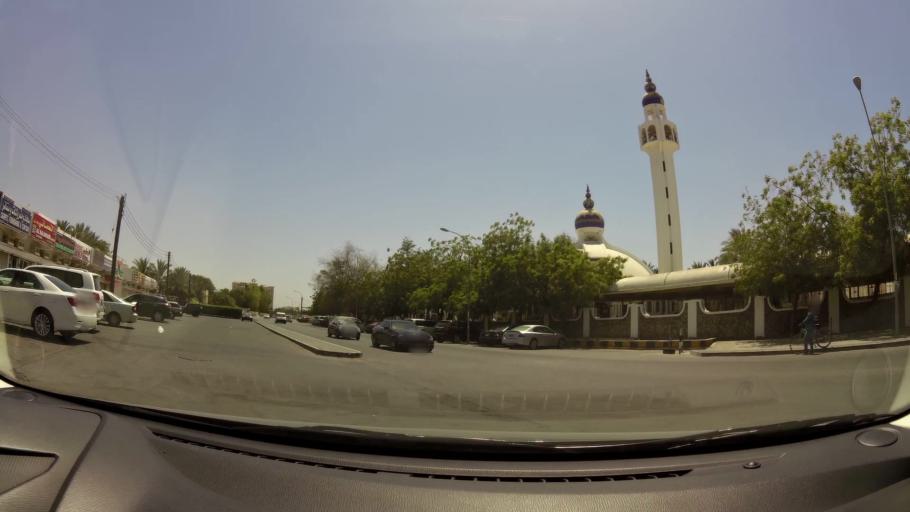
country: OM
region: Muhafazat Masqat
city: As Sib al Jadidah
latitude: 23.6330
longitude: 58.2300
